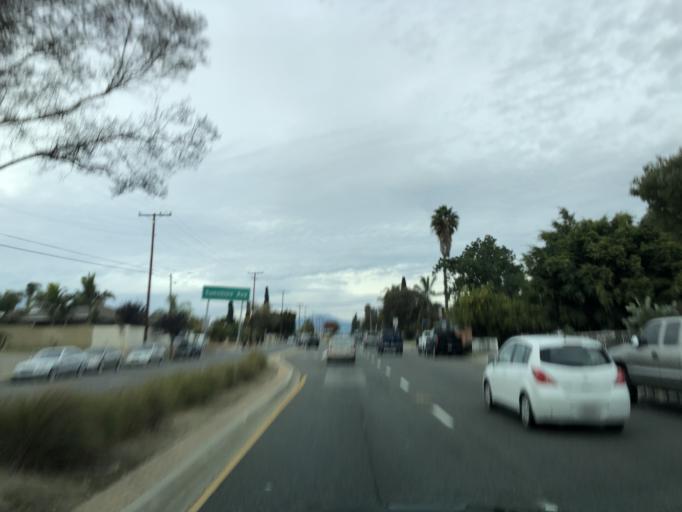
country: US
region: California
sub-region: Los Angeles County
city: La Mirada
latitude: 33.9210
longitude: -118.0465
